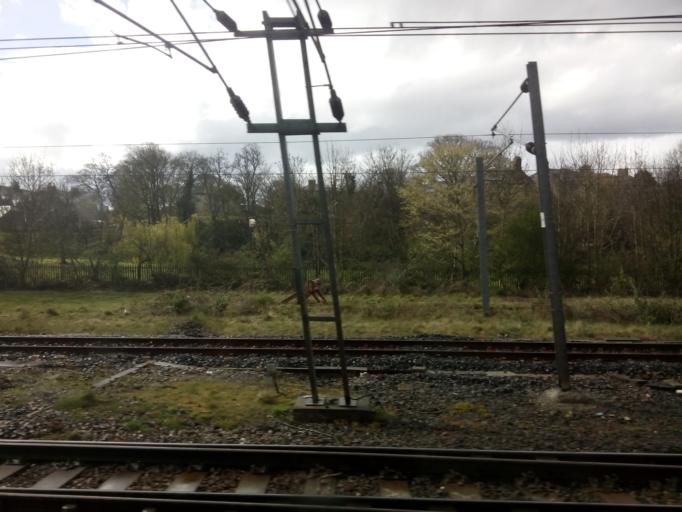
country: GB
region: England
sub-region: Northumberland
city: Berwick-Upon-Tweed
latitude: 55.7758
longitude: -2.0092
